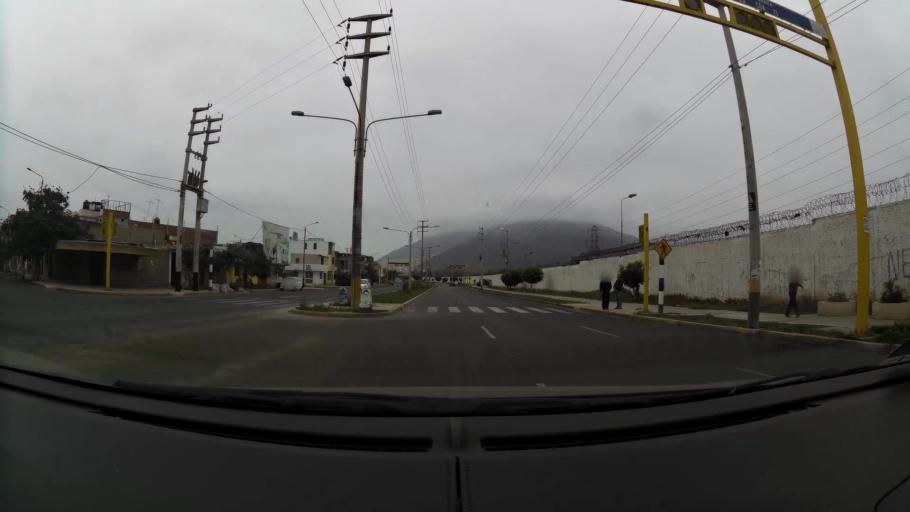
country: PE
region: Ancash
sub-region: Provincia de Santa
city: Chimbote
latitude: -9.0640
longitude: -78.5910
